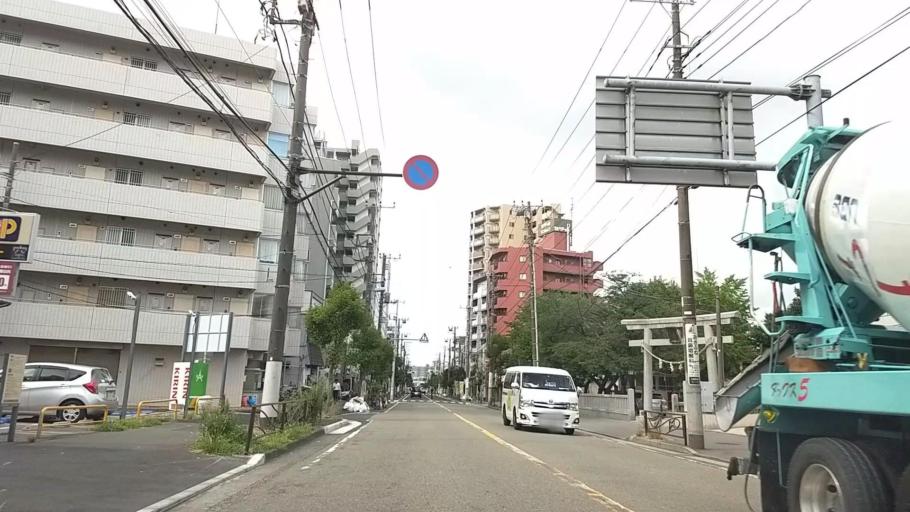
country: JP
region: Kanagawa
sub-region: Kawasaki-shi
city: Kawasaki
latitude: 35.5352
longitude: 139.7256
